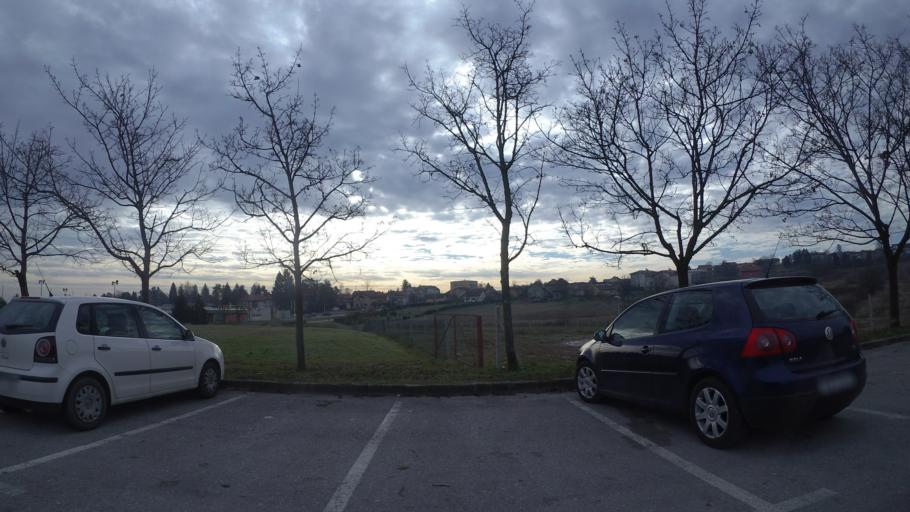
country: HR
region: Karlovacka
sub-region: Grad Karlovac
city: Karlovac
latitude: 45.4764
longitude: 15.5411
